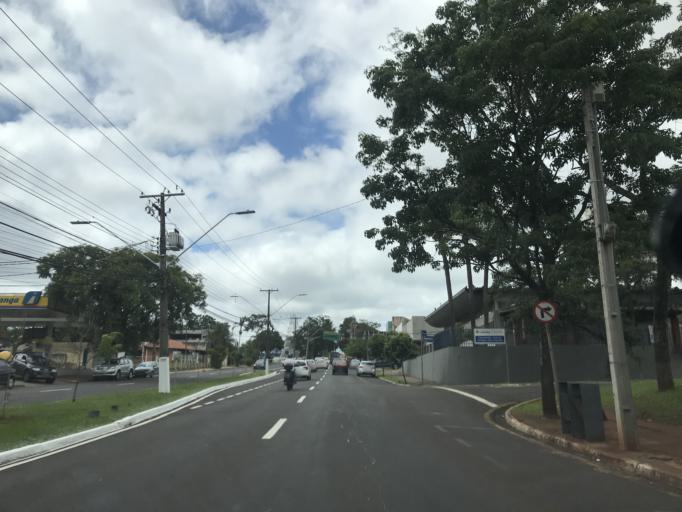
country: BR
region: Parana
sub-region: Londrina
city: Londrina
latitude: -23.3333
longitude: -51.1678
